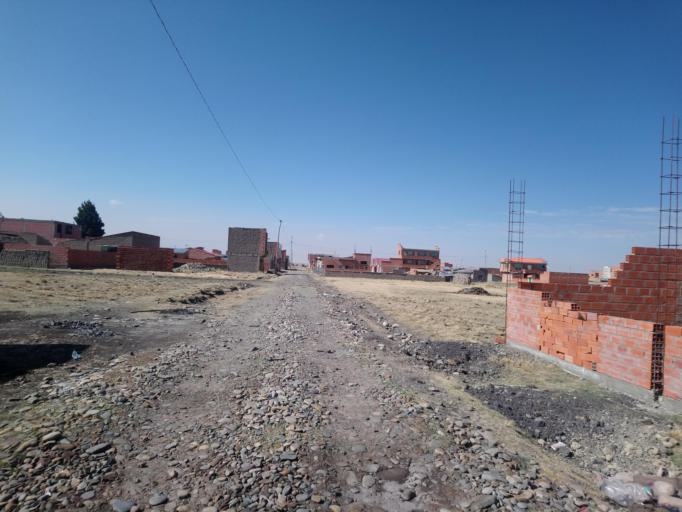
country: BO
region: La Paz
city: Batallas
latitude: -16.4374
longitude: -68.3749
